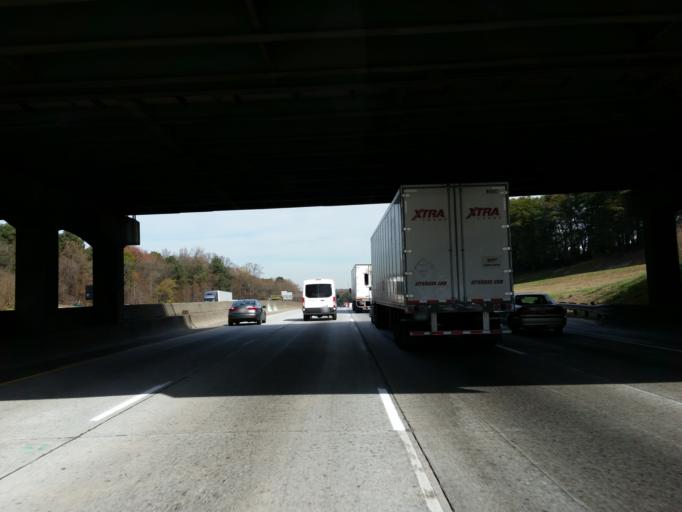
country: US
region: Georgia
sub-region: Cobb County
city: Vinings
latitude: 33.7866
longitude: -84.4932
